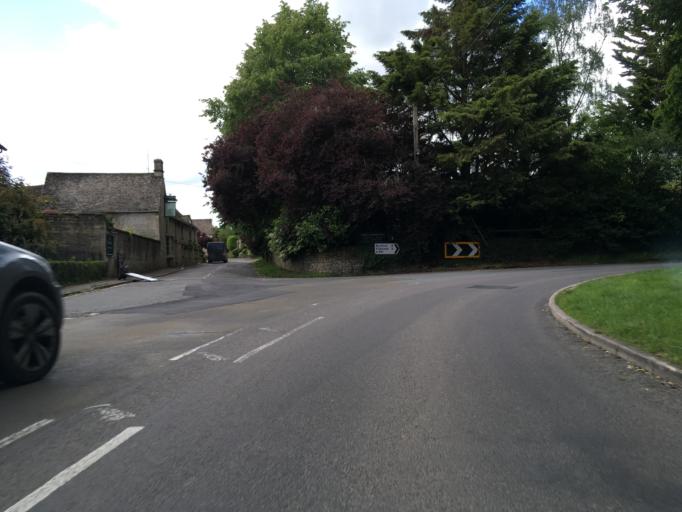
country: GB
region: England
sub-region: Oxfordshire
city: Shipton under Wychwood
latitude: 51.8546
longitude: -1.5996
